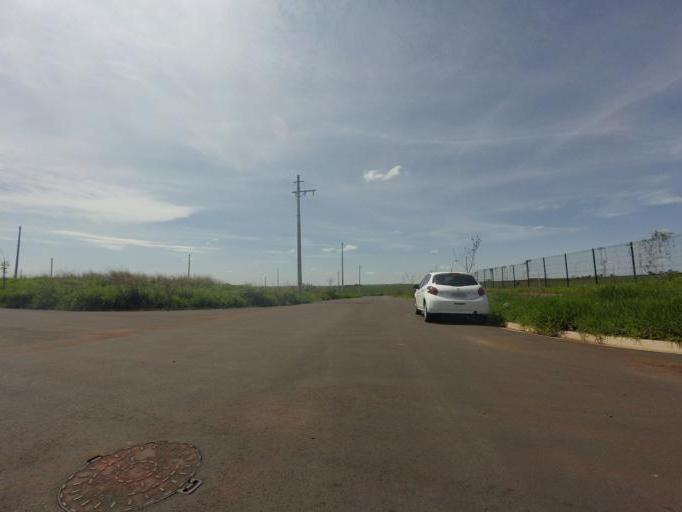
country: BR
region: Sao Paulo
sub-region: Piracicaba
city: Piracicaba
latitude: -22.7615
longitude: -47.5817
